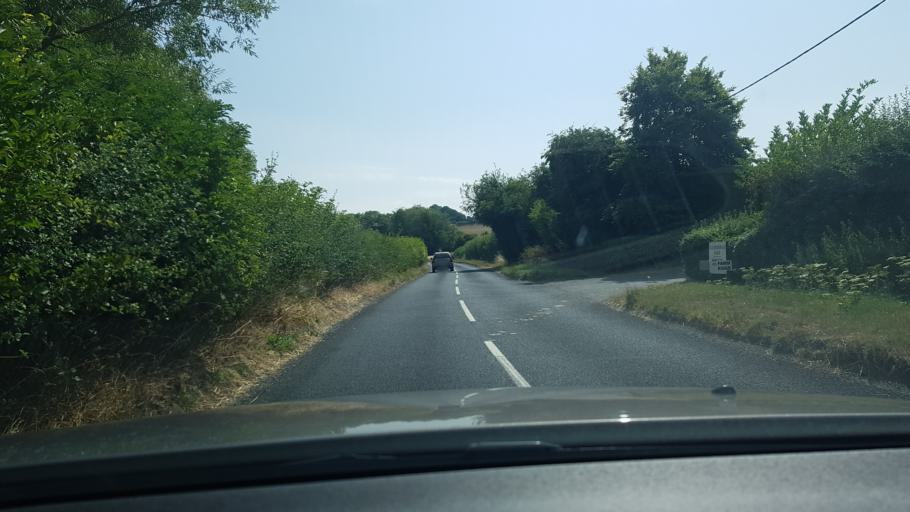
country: GB
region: England
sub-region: West Berkshire
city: Lambourn
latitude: 51.4902
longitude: -1.4945
